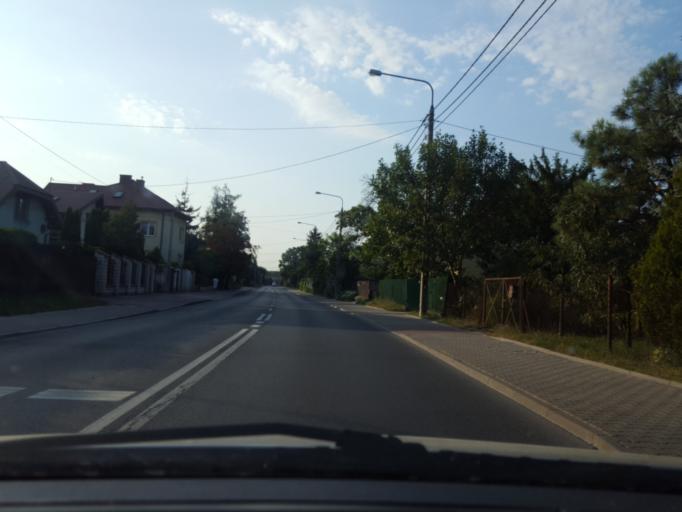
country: PL
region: Masovian Voivodeship
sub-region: Warszawa
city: Rembertow
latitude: 52.2670
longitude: 21.1541
